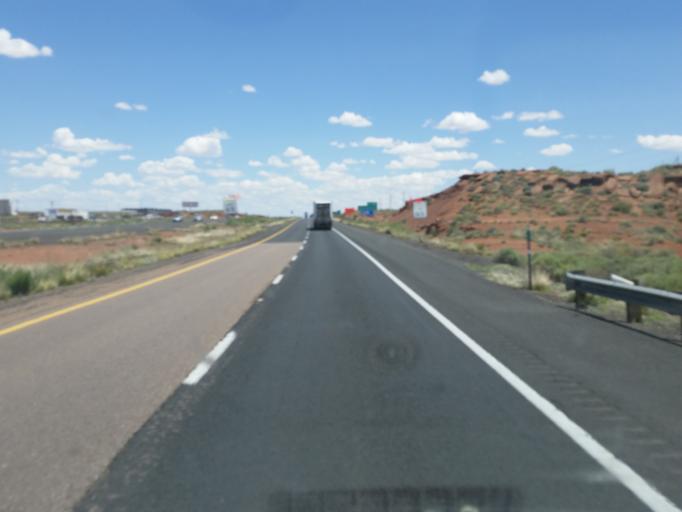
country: US
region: Arizona
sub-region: Navajo County
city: Holbrook
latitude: 34.9097
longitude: -110.2333
